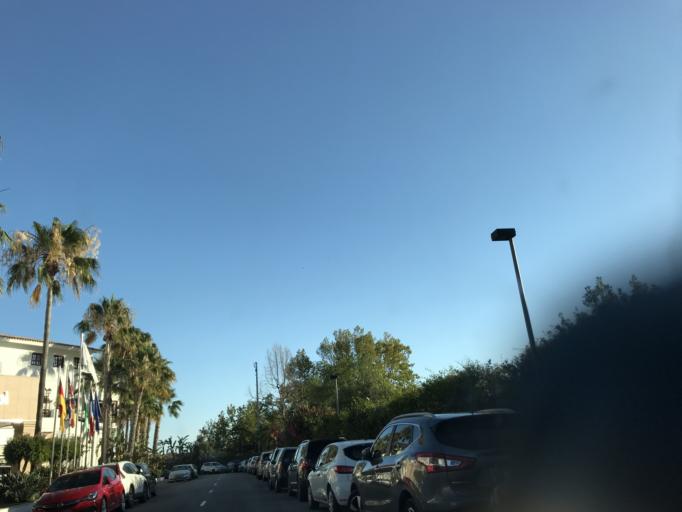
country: ES
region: Andalusia
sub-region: Provincia de Malaga
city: Benahavis
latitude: 36.4575
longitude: -5.0480
